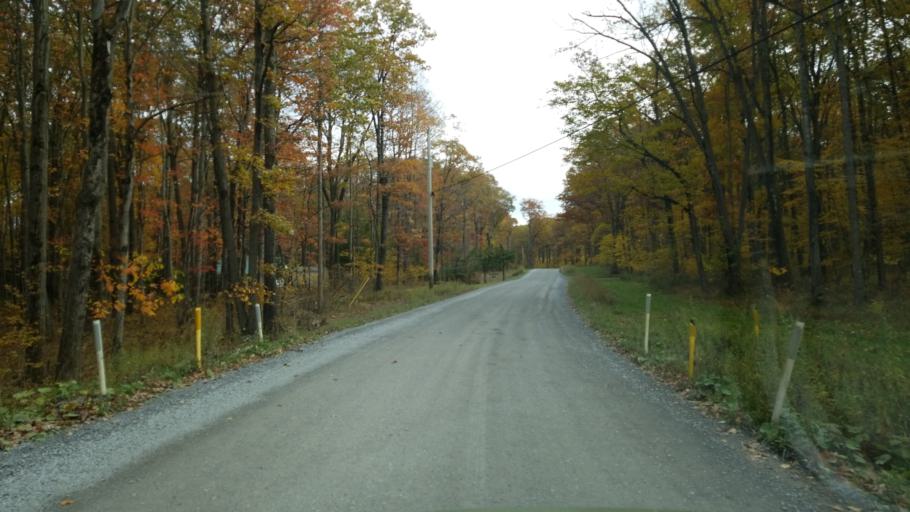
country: US
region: Pennsylvania
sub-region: Clearfield County
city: Clearfield
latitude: 41.1437
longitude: -78.4914
